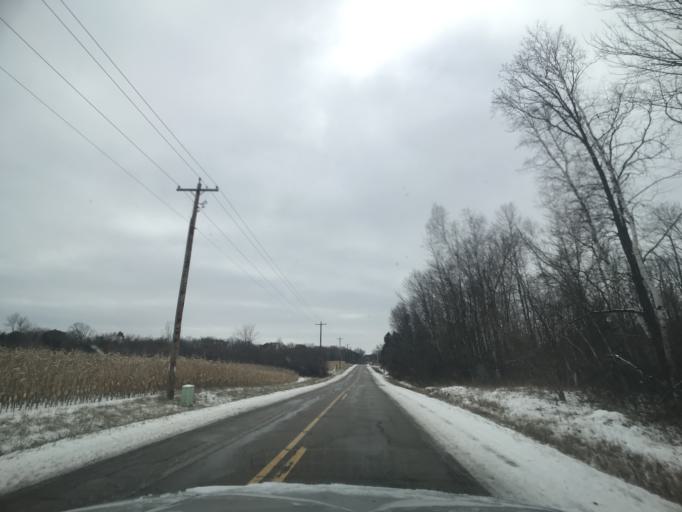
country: US
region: Wisconsin
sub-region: Brown County
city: Suamico
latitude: 44.7155
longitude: -88.0709
